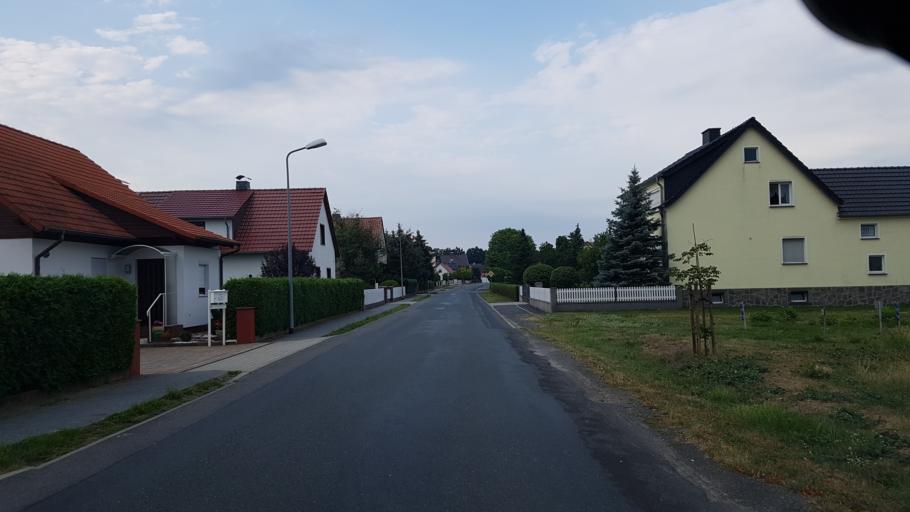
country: DE
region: Brandenburg
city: Lindenau
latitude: 51.4034
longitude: 13.7228
